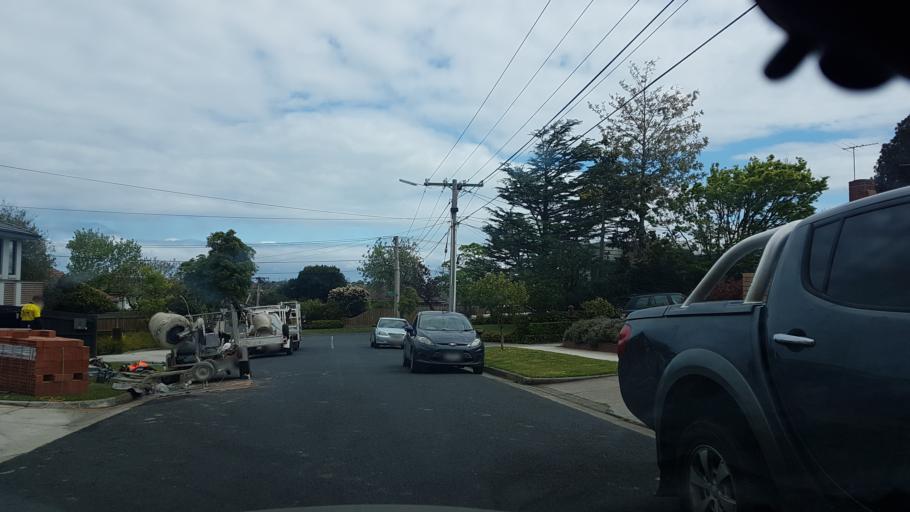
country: AU
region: Victoria
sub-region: Bayside
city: Moorabbin
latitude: -37.9295
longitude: 145.0453
